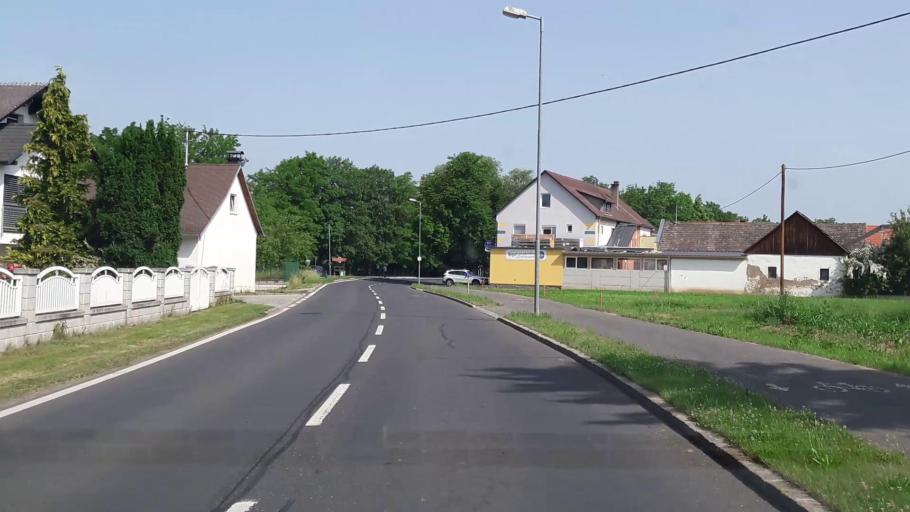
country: AT
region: Styria
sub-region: Politischer Bezirk Hartberg-Fuerstenfeld
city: Burgau
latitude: 47.1348
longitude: 16.1150
